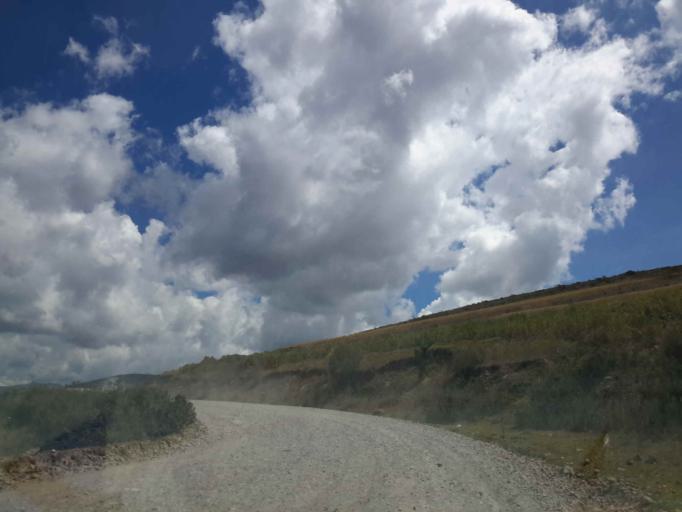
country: PE
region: Apurimac
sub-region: Provincia de Andahuaylas
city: San Jeronimo
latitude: -13.6394
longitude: -73.3345
